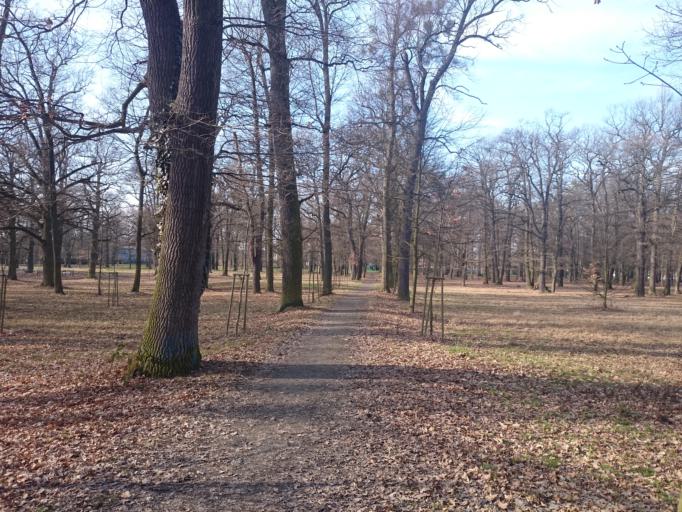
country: CZ
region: Pardubicky
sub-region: Okres Chrudim
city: Hermanuv Mestec
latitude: 49.9480
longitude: 15.6776
